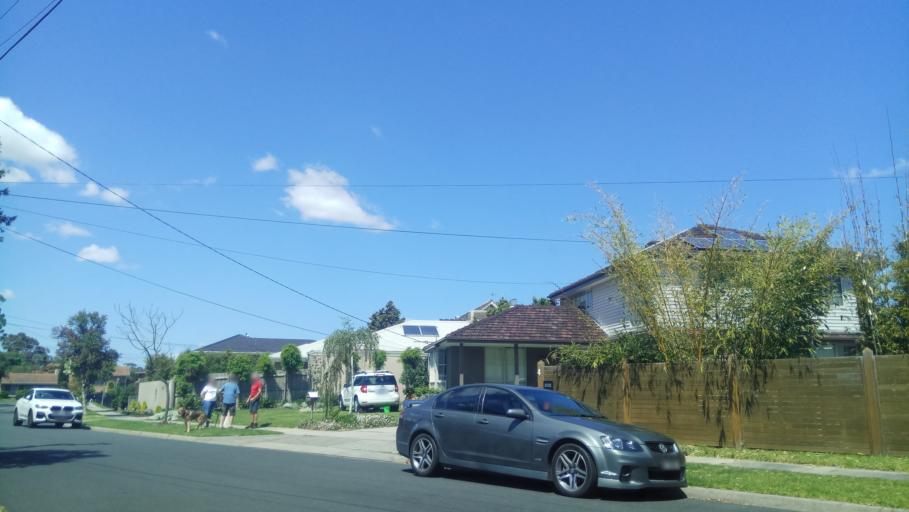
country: AU
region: Victoria
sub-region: Kingston
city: Dingley Village
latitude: -37.9851
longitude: 145.1368
